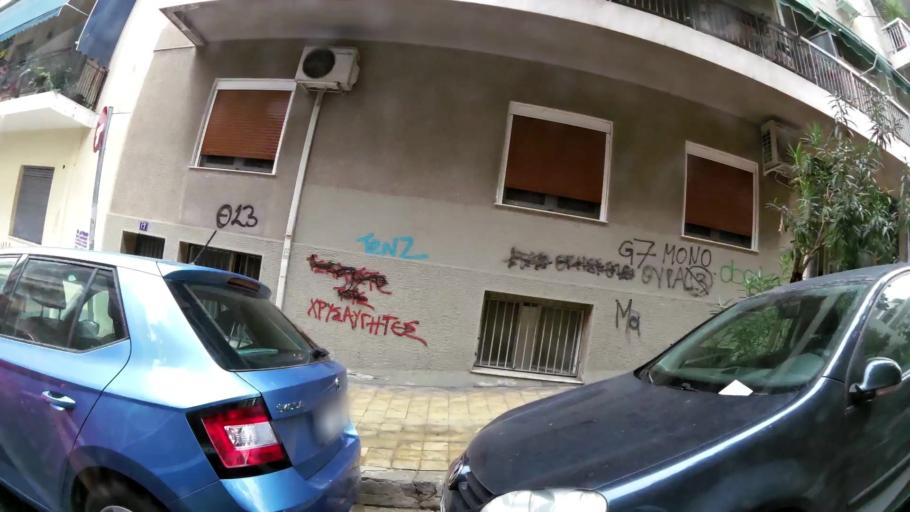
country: GR
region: Attica
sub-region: Nomarchia Athinas
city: Vyronas
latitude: 37.9710
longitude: 23.7440
